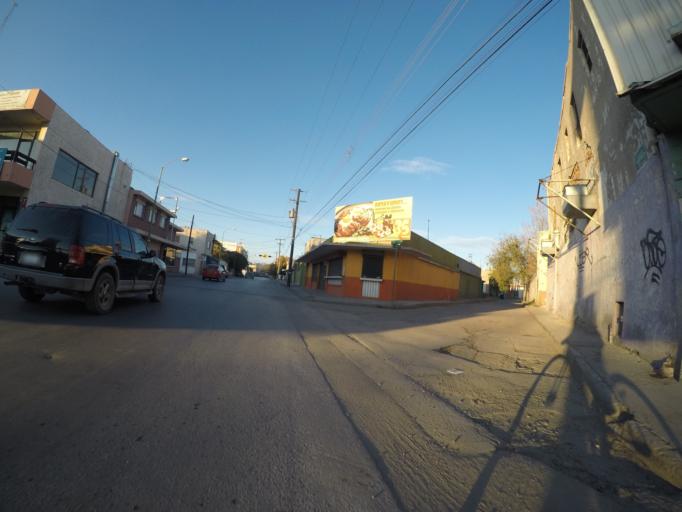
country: MX
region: Chihuahua
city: Ciudad Juarez
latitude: 31.7359
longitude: -106.4779
